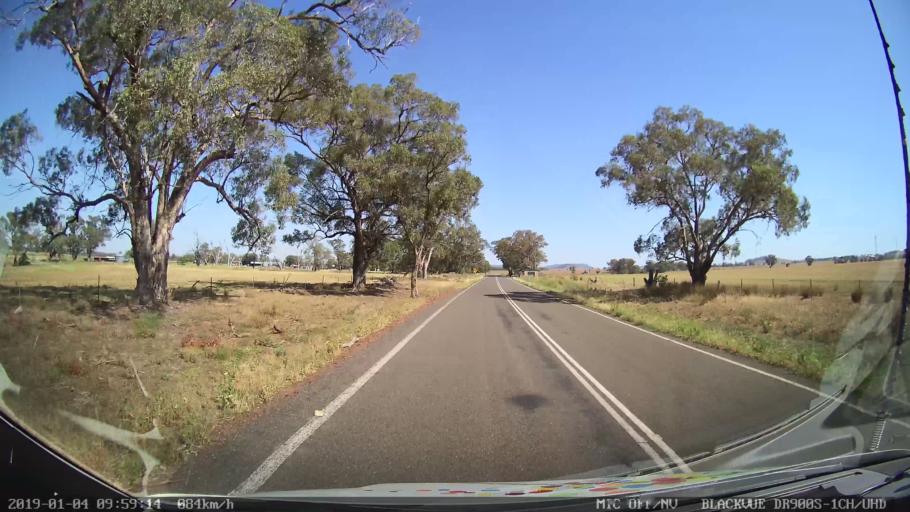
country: AU
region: New South Wales
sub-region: Cabonne
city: Canowindra
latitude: -33.5098
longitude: 148.3877
